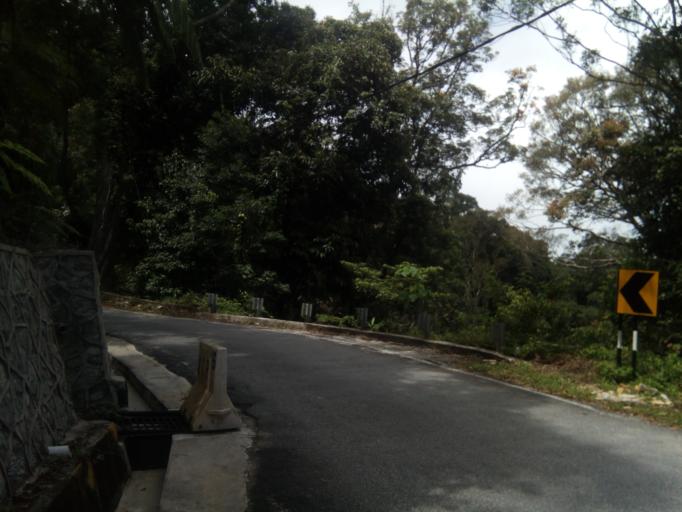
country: MY
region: Penang
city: Tanjung Tokong
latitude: 5.4263
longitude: 100.2717
